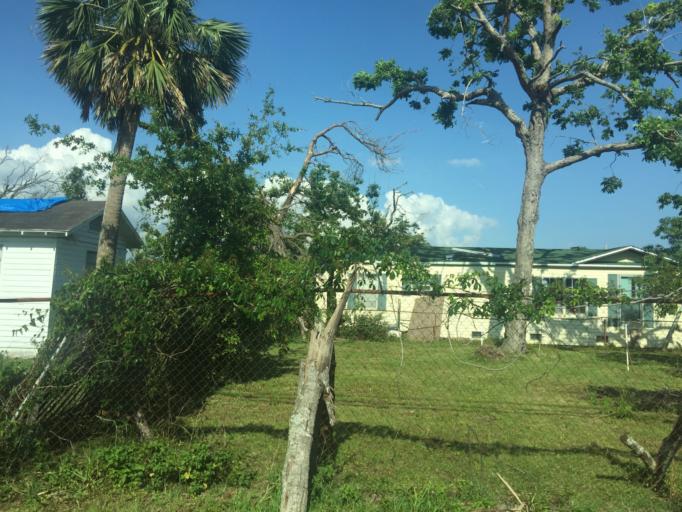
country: US
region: Florida
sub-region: Bay County
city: Springfield
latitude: 30.1516
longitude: -85.6191
